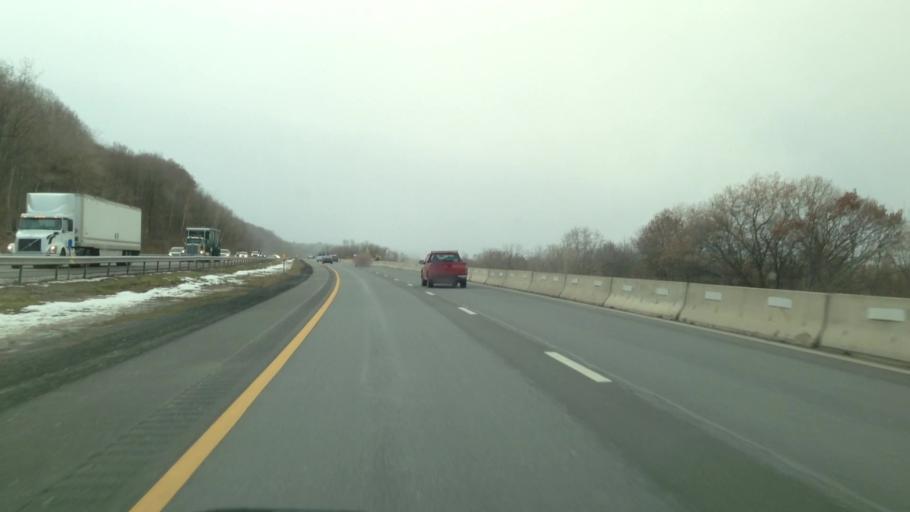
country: US
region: New York
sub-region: Schenectady County
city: Scotia
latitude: 42.8719
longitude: -74.0499
